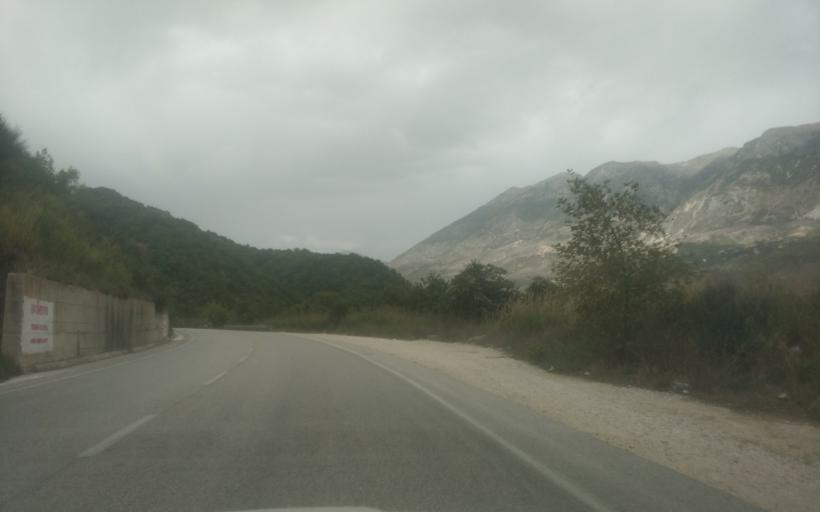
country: AL
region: Gjirokaster
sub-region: Rrethi i Gjirokastres
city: Picar
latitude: 40.2148
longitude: 20.0870
